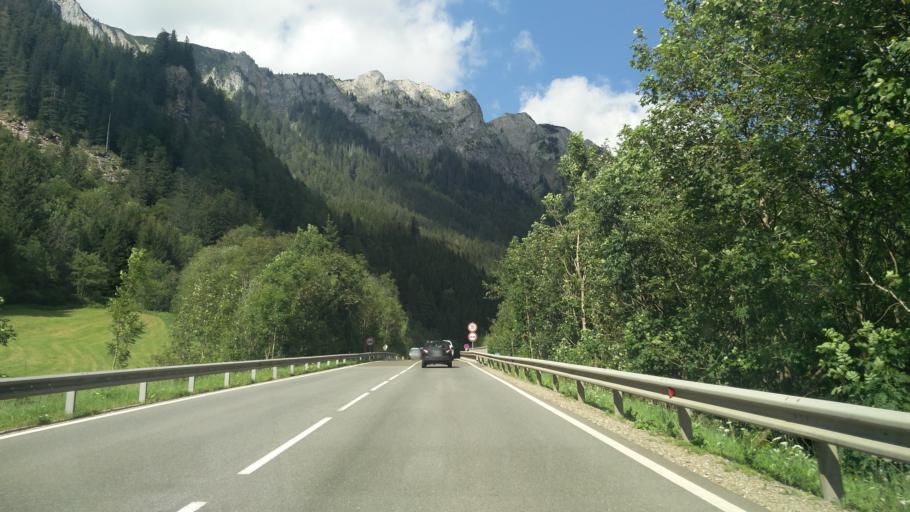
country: AT
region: Styria
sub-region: Politischer Bezirk Leoben
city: Eisenerz
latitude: 47.5483
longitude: 14.9311
